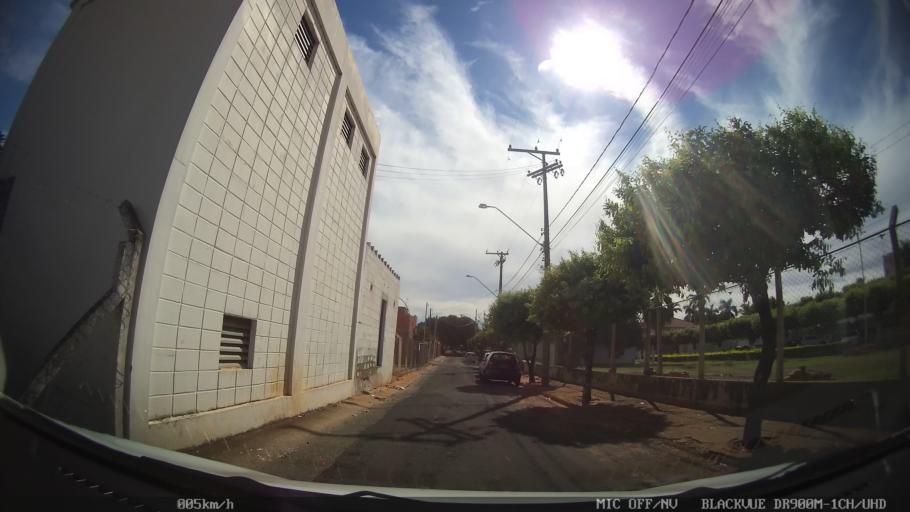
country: BR
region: Sao Paulo
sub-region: Catanduva
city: Catanduva
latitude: -21.1270
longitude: -48.9602
